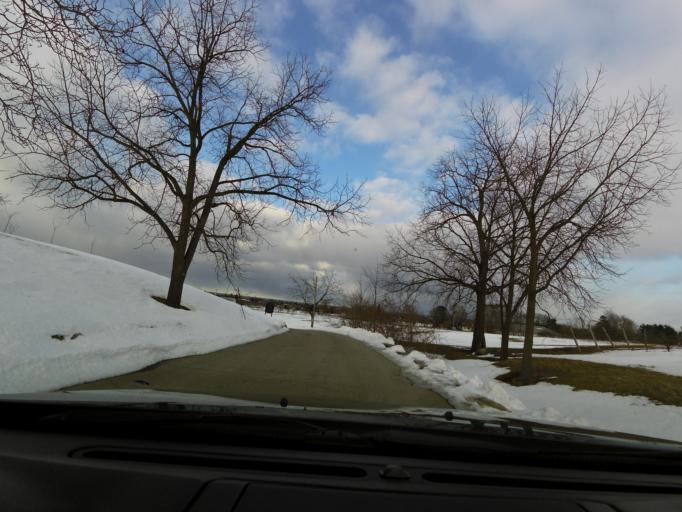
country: CA
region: Ontario
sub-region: Regional Municipality of Niagara
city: St. Catharines
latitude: 43.1766
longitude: -79.5082
